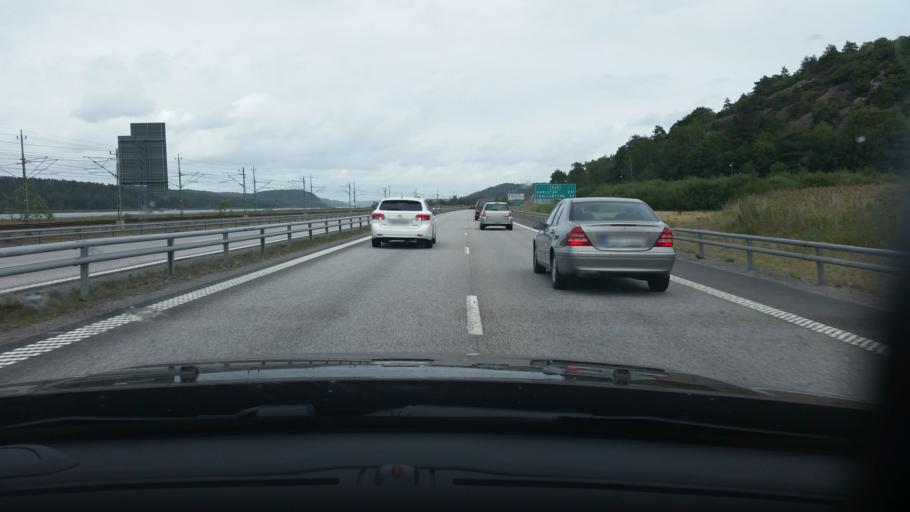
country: SE
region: Vaestra Goetaland
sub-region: Ale Kommun
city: Surte
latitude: 57.8642
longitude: 12.0206
